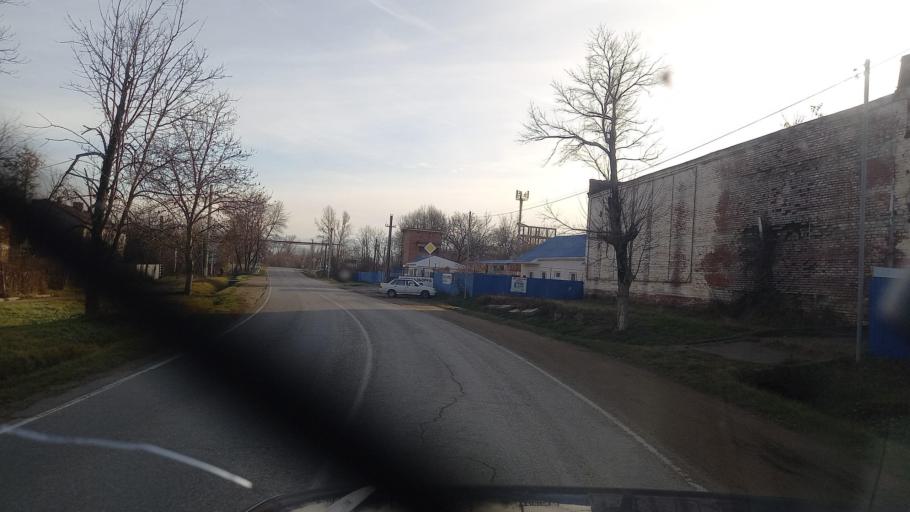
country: RU
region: Krasnodarskiy
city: Khadyzhensk
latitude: 44.4449
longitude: 39.5245
